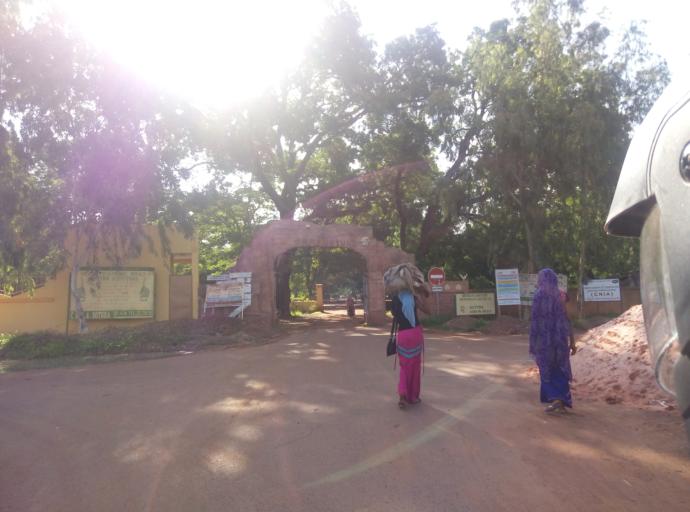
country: ML
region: Bamako
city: Bamako
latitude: 12.6539
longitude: -7.9293
